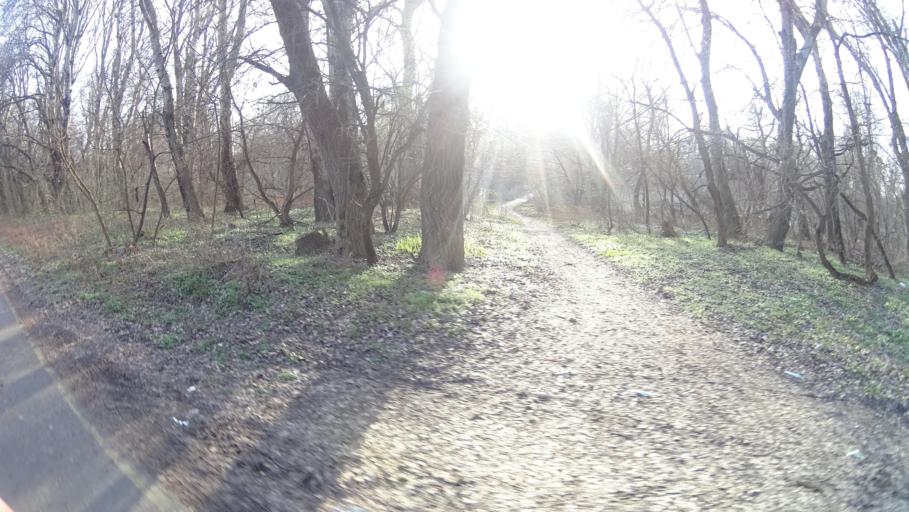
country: HU
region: Pest
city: Vac
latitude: 47.7547
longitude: 19.1367
